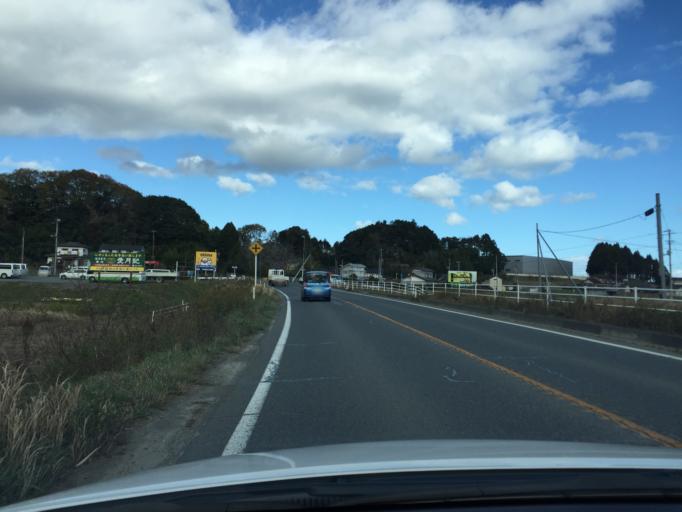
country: JP
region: Fukushima
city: Namie
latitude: 37.6079
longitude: 141.0070
